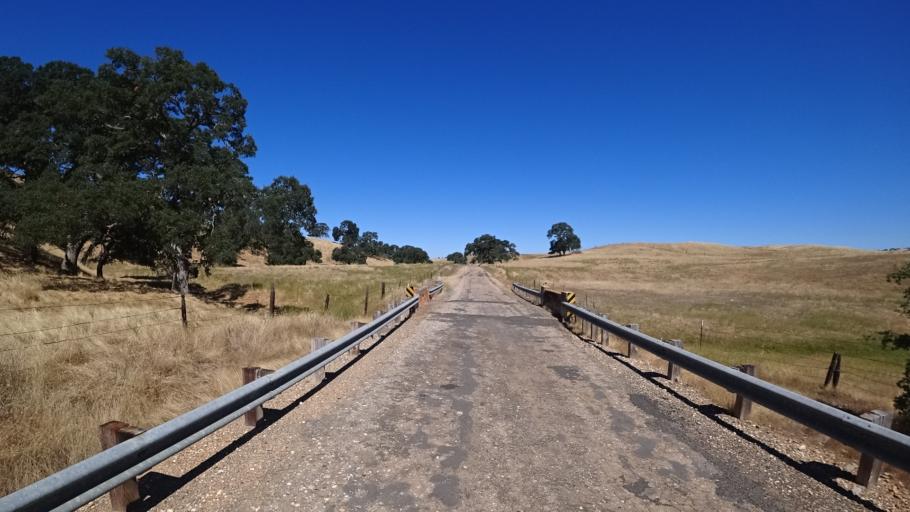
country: US
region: California
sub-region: Calaveras County
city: Rancho Calaveras
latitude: 38.0234
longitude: -120.8391
